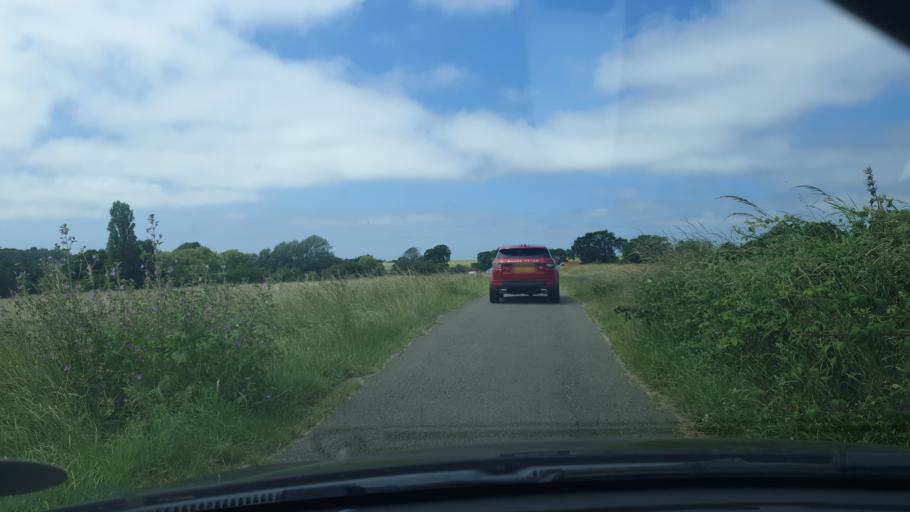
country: GB
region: England
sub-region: Essex
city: Frinton-on-Sea
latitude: 51.8337
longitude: 1.2364
